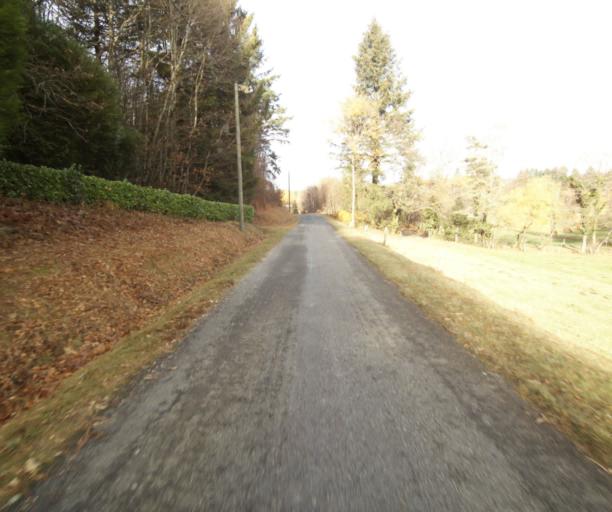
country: FR
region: Limousin
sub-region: Departement de la Correze
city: Sainte-Fortunade
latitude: 45.1931
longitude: 1.7380
